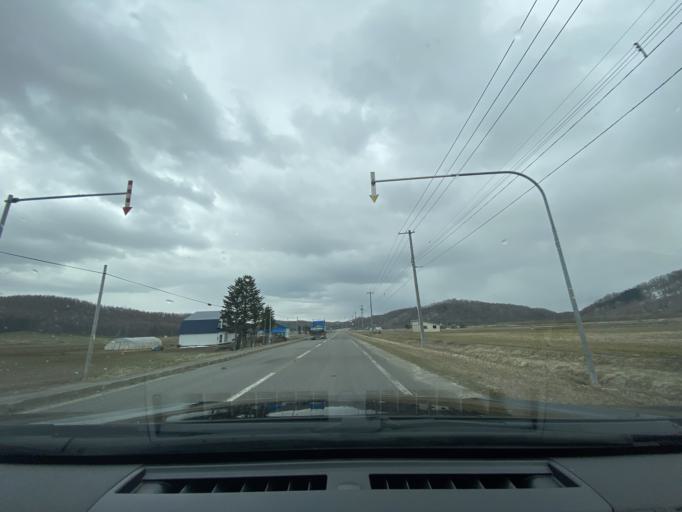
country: JP
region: Hokkaido
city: Nayoro
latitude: 44.1800
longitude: 142.2896
